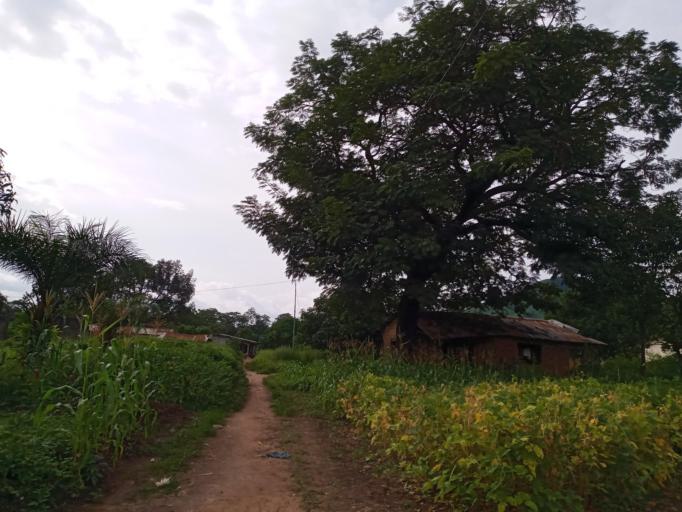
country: SL
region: Northern Province
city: Bumbuna
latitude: 9.0508
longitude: -11.7520
